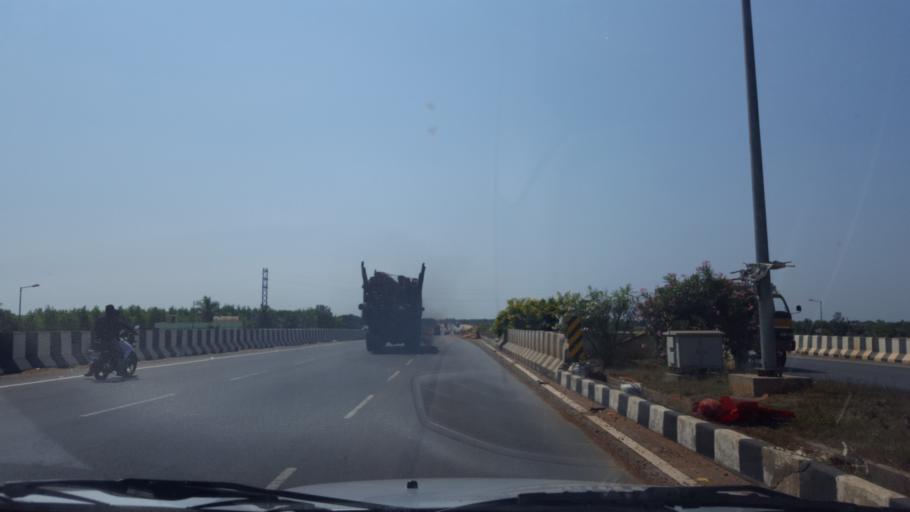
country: IN
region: Andhra Pradesh
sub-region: Prakasam
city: Singarayakonda
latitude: 15.2788
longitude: 80.0253
